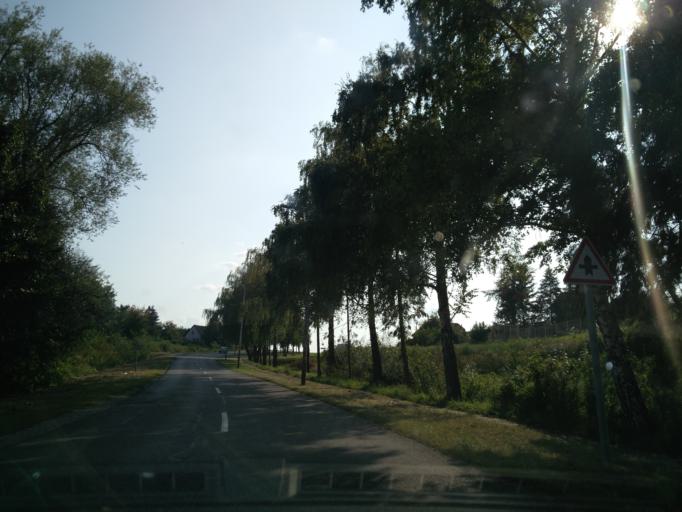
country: HU
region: Zala
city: Zalaegerszeg
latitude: 46.8594
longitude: 16.8457
